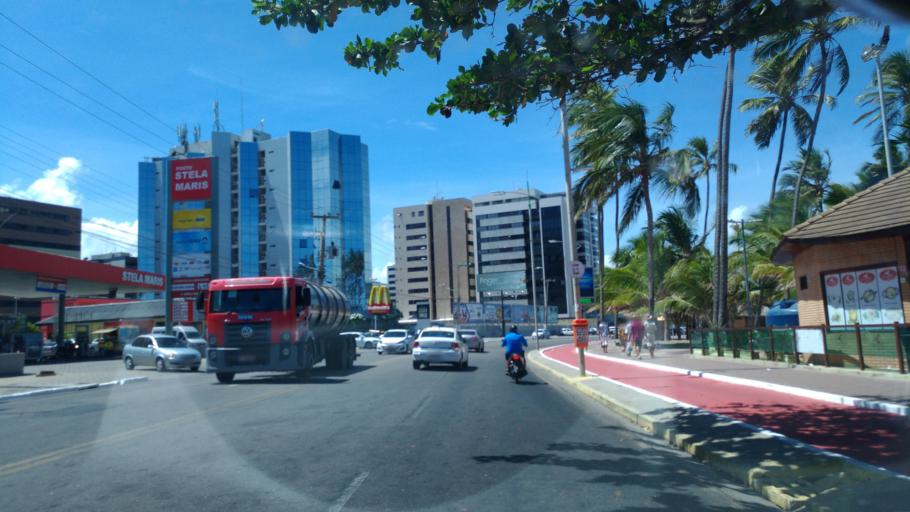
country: BR
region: Alagoas
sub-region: Maceio
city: Maceio
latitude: -9.6493
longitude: -35.7002
